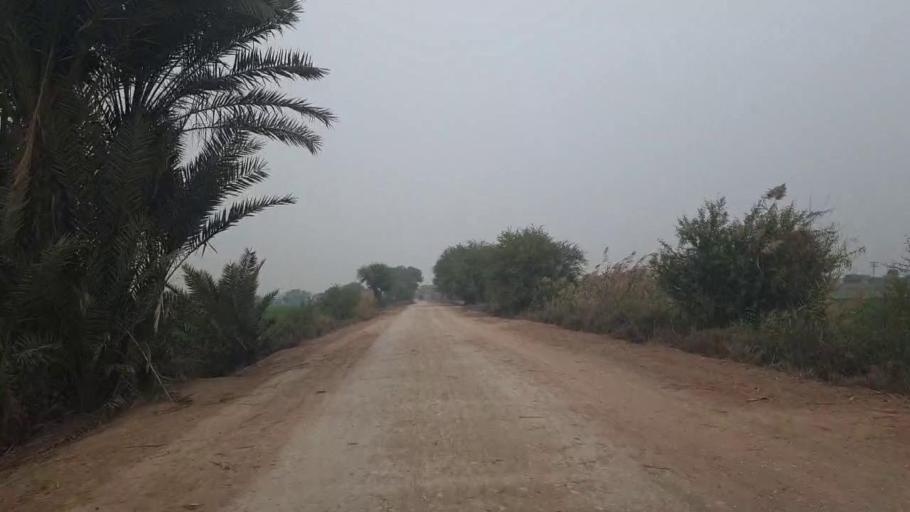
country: PK
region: Sindh
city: Tando Adam
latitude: 25.7769
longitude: 68.6985
